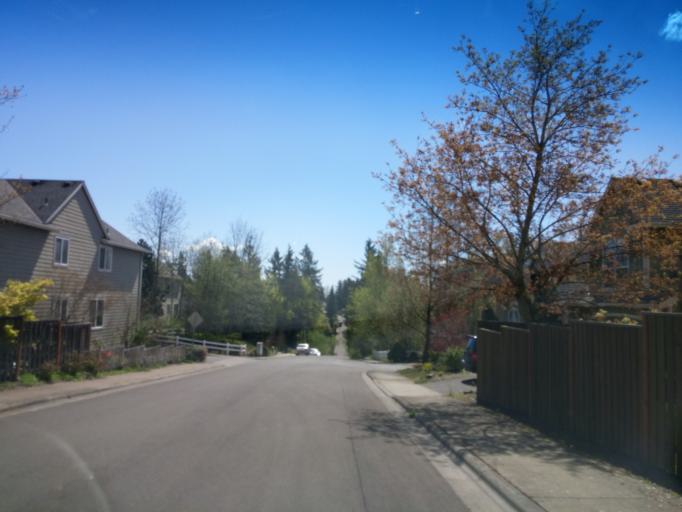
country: US
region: Oregon
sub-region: Washington County
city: West Haven
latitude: 45.5329
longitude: -122.7825
